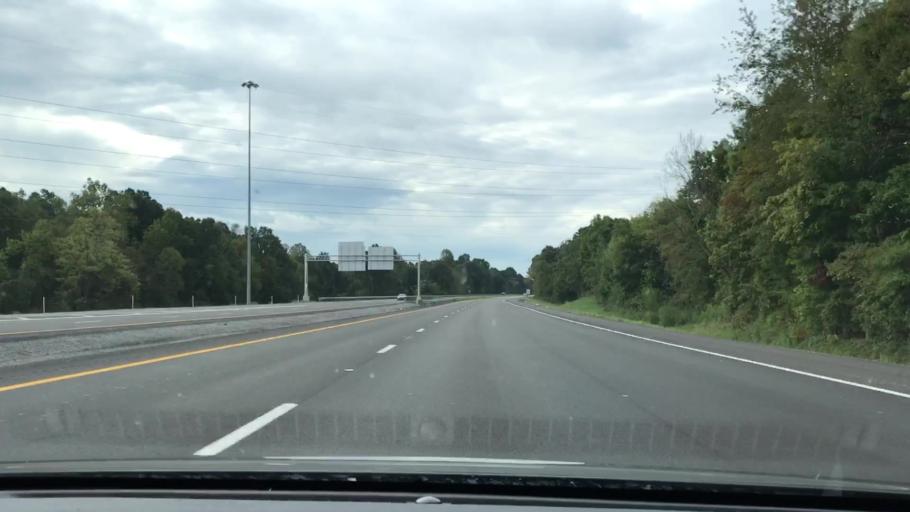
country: US
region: Kentucky
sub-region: Marshall County
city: Calvert City
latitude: 36.9810
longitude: -88.3459
